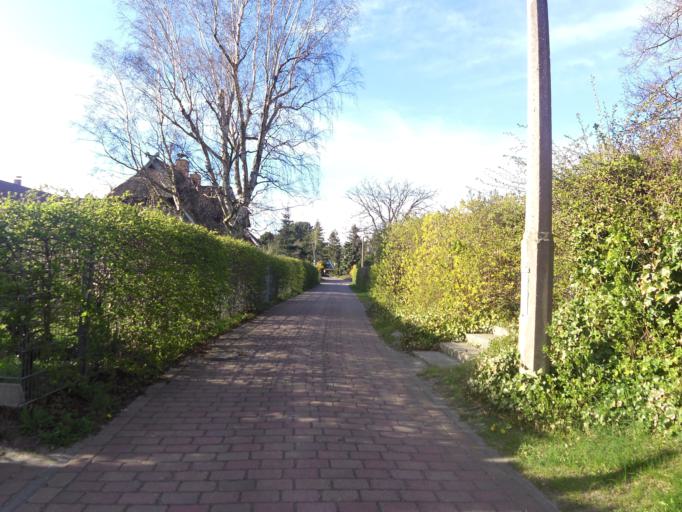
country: DE
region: Mecklenburg-Vorpommern
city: Zingst
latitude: 54.4387
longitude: 12.6884
